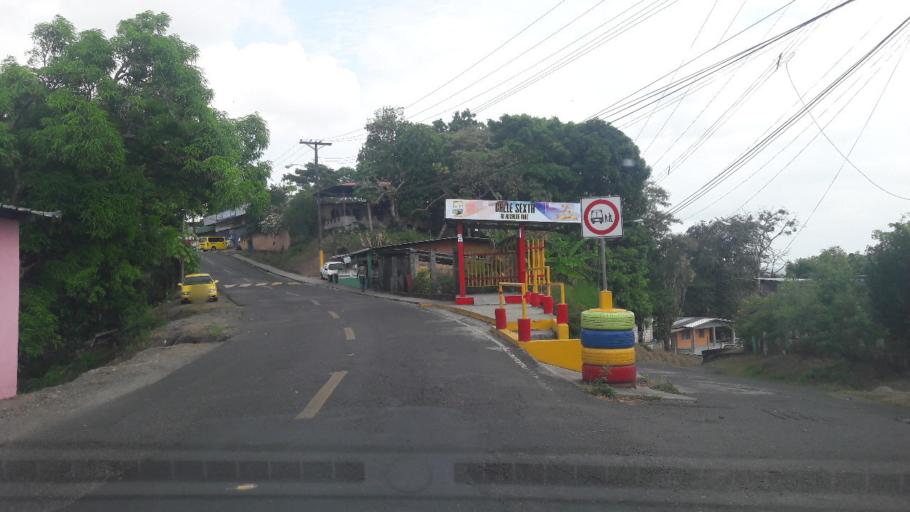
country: PA
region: Panama
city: Alcalde Diaz
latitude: 9.1246
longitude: -79.5561
